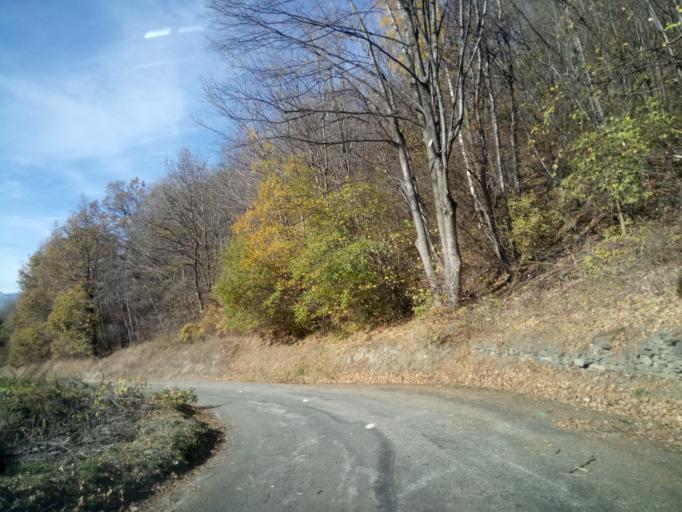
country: FR
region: Rhone-Alpes
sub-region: Departement de la Savoie
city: Saint-Michel-de-Maurienne
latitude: 45.2273
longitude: 6.4797
